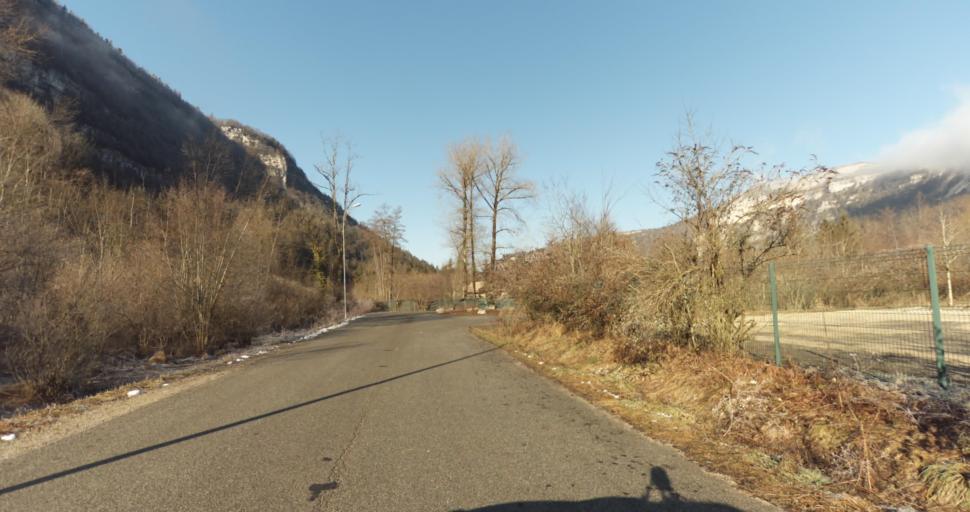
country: FR
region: Rhone-Alpes
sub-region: Departement de l'Ain
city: Nantua
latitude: 46.1484
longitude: 5.6045
